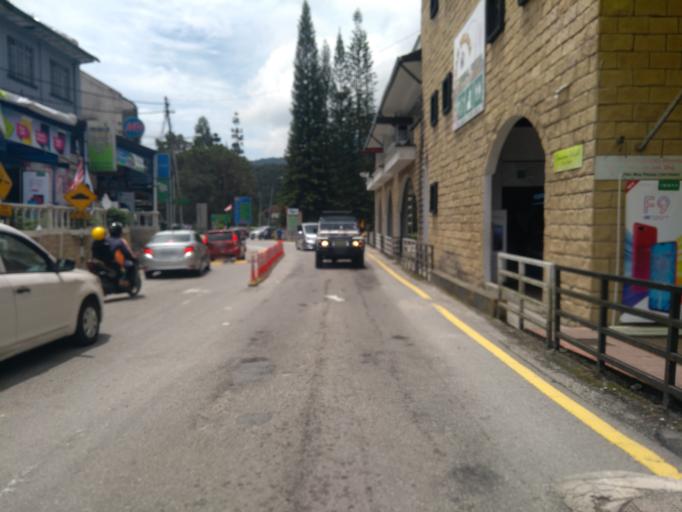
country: MY
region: Pahang
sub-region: Cameron Highlands
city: Tanah Rata
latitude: 4.4708
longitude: 101.3787
